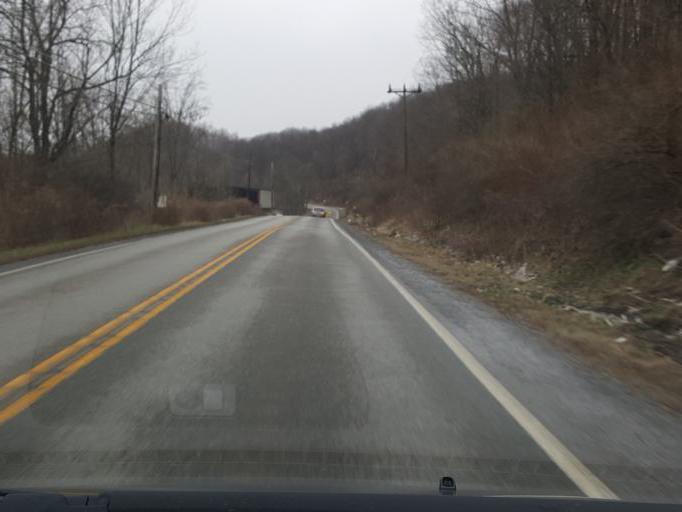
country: US
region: Pennsylvania
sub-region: Blair County
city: Greenwood
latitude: 40.5504
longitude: -78.3644
